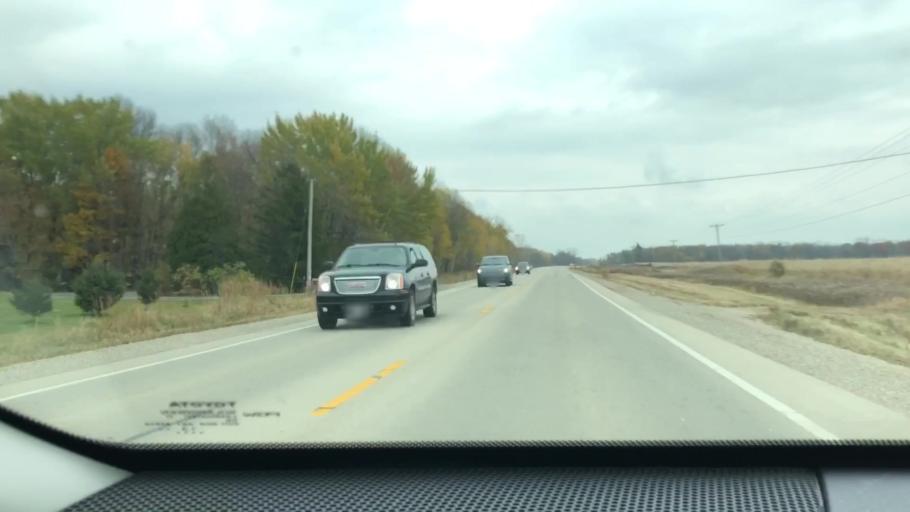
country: US
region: Wisconsin
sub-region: Brown County
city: Oneida
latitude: 44.5025
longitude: -88.2472
